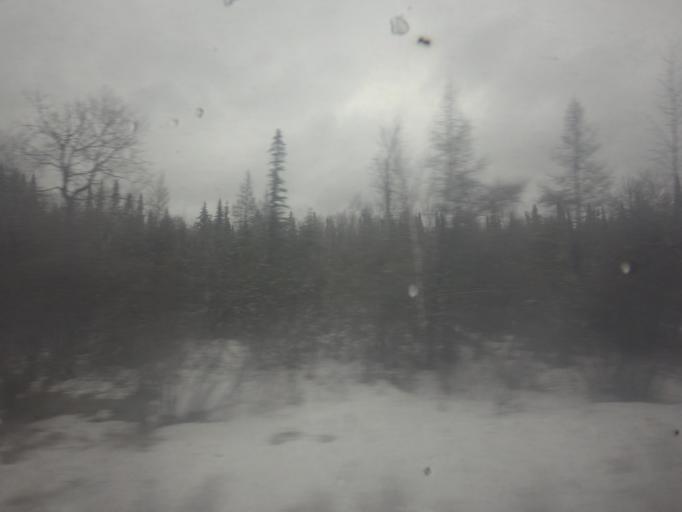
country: CA
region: Ontario
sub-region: Lanark County
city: Smiths Falls
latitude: 45.0033
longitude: -75.9604
